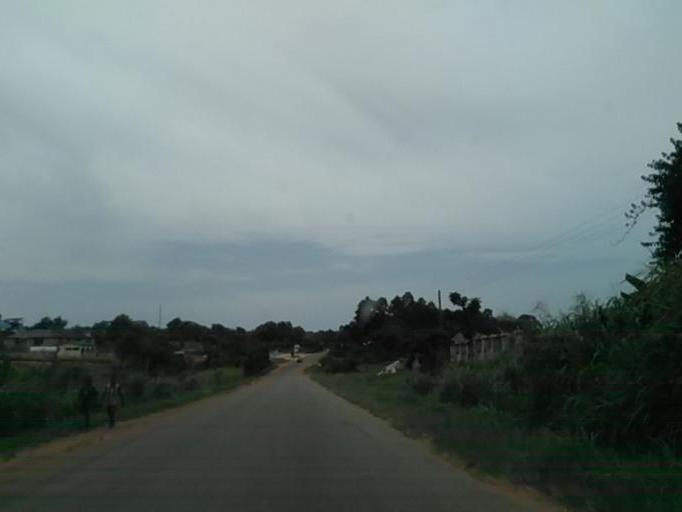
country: GH
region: Ashanti
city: Mampong
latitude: 7.0758
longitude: -1.4103
